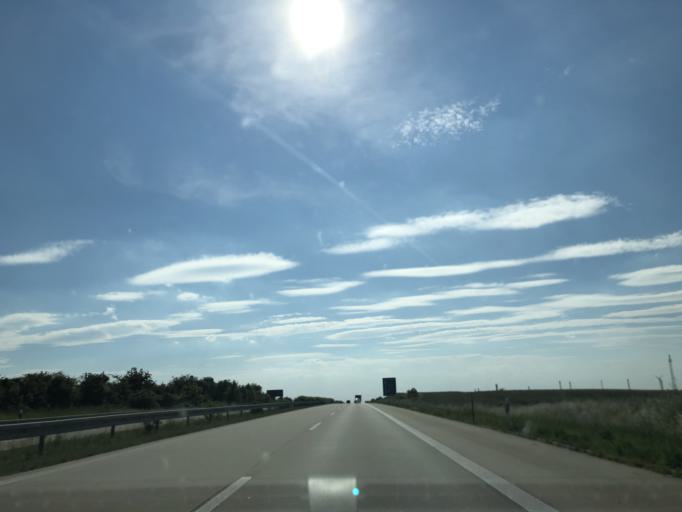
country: DE
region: Mecklenburg-Vorpommern
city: Penkun
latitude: 53.3178
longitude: 14.2867
